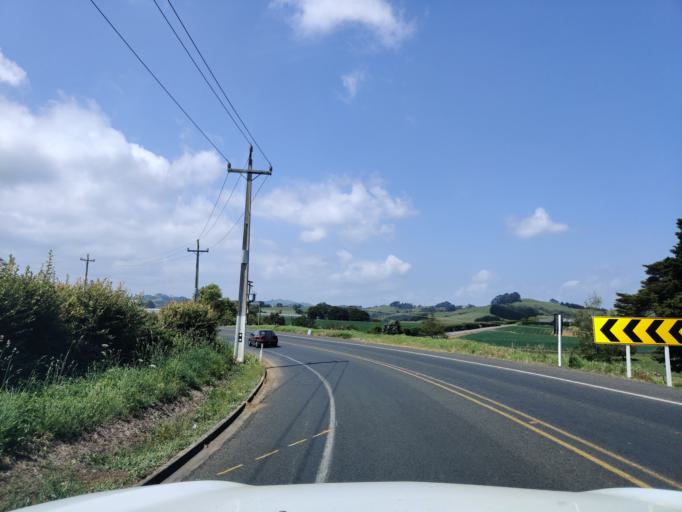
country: NZ
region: Auckland
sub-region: Auckland
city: Pukekohe East
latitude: -37.2390
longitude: 174.9584
